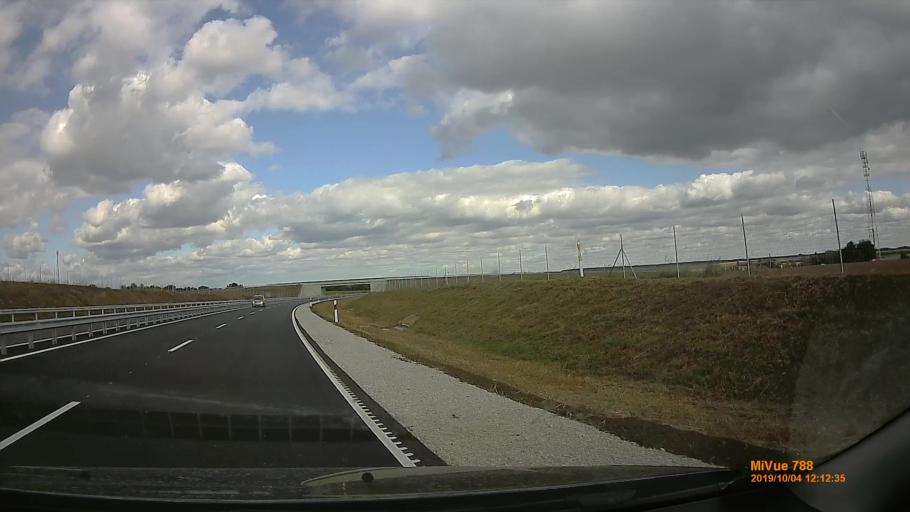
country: HU
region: Somogy
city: Kaposvar
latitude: 46.5106
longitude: 17.8090
